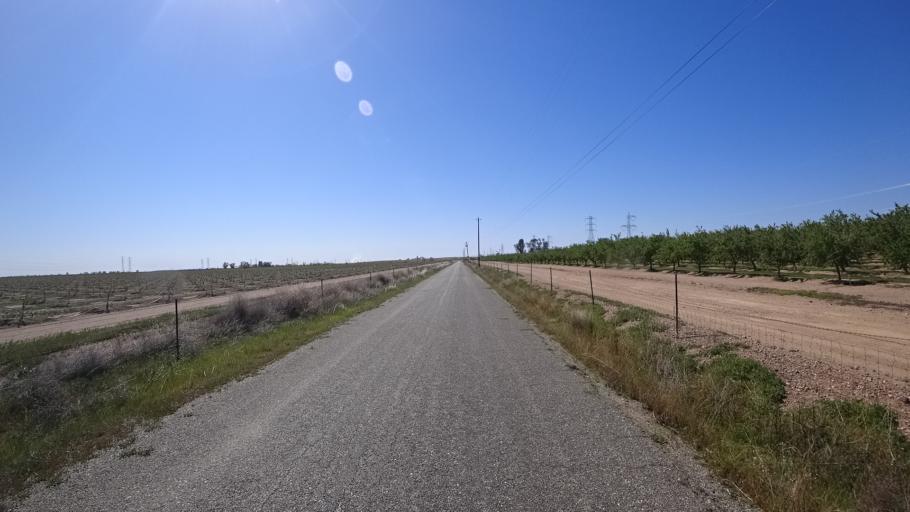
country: US
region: California
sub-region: Glenn County
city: Orland
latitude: 39.6584
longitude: -122.2719
